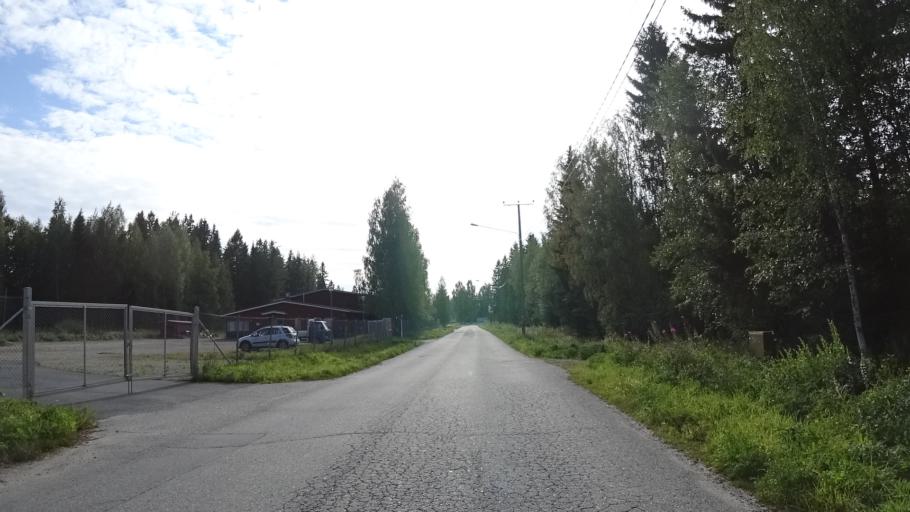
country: FI
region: North Karelia
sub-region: Joensuu
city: Eno
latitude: 62.7974
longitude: 30.1429
